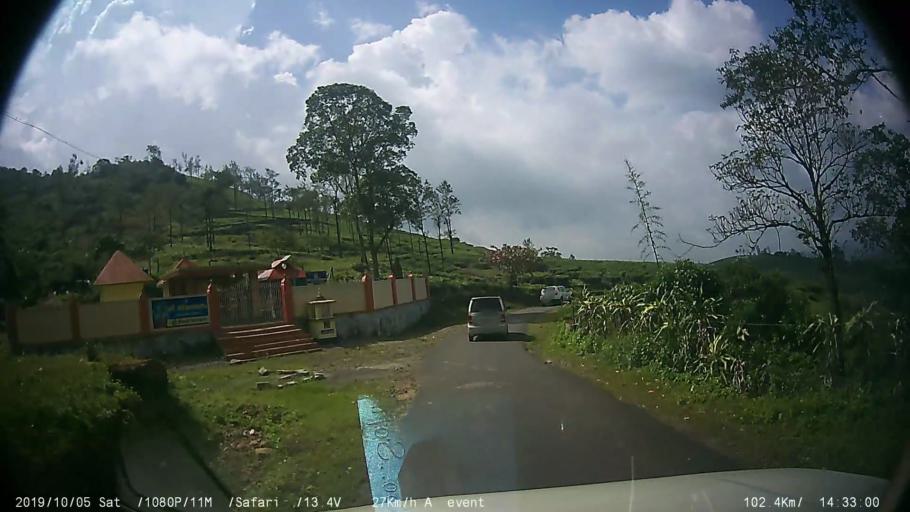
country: IN
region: Kerala
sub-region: Kottayam
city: Erattupetta
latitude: 9.6138
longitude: 76.9676
